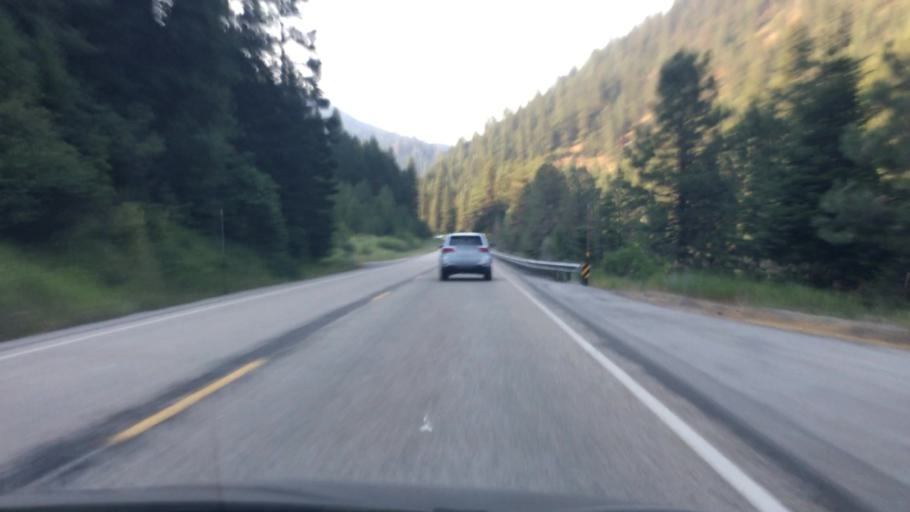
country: US
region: Idaho
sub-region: Valley County
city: Cascade
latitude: 44.1605
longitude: -116.1180
